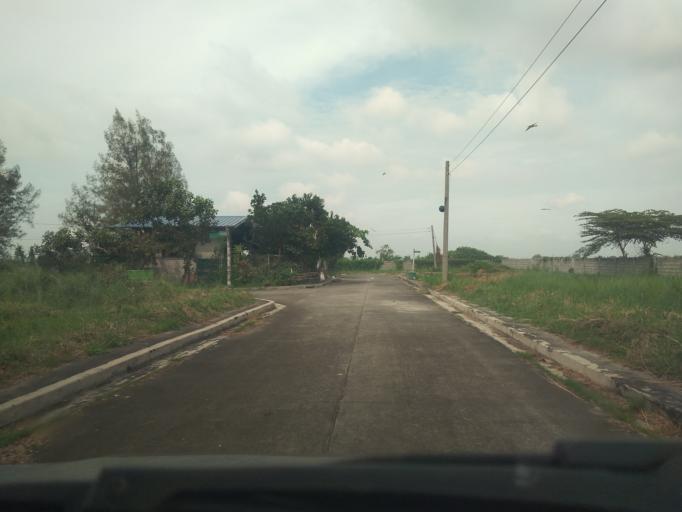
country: PH
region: Central Luzon
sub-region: Province of Pampanga
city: Santo Domingo
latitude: 15.0048
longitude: 120.7260
